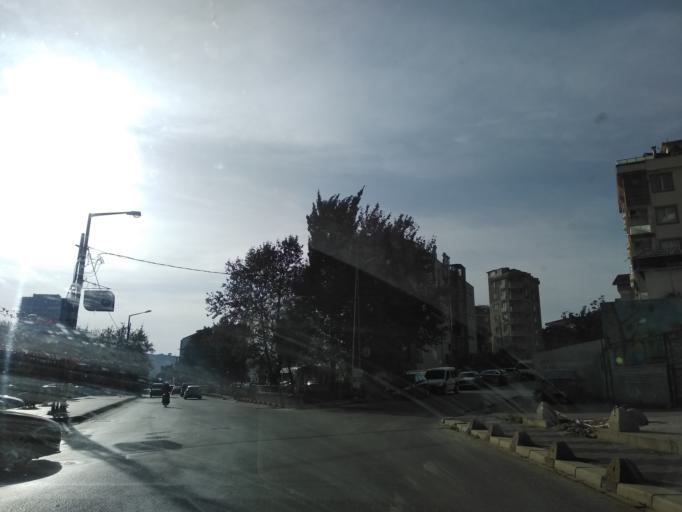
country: TR
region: Istanbul
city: Maltepe
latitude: 40.9177
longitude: 29.1594
